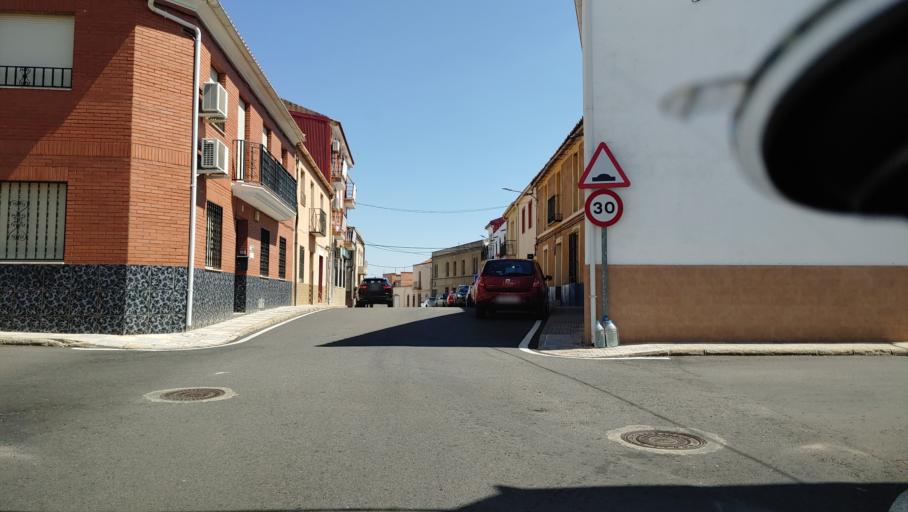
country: ES
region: Castille-La Mancha
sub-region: Provincia de Ciudad Real
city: Alamillo
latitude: 38.7377
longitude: -4.7118
